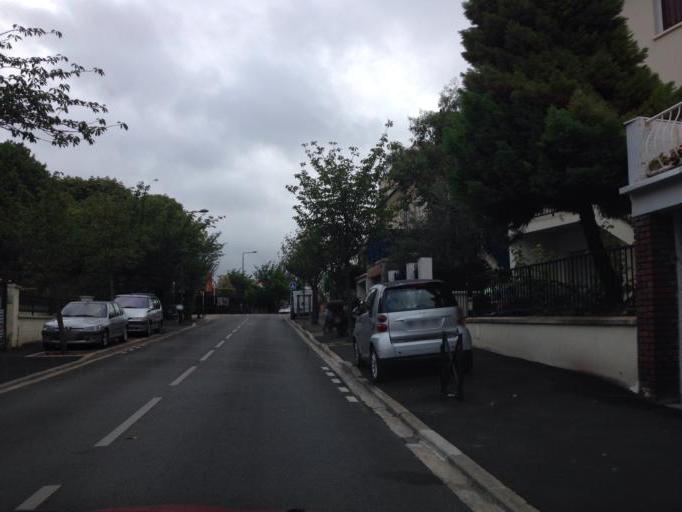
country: FR
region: Ile-de-France
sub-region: Departement des Hauts-de-Seine
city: Meudon
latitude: 48.8134
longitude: 2.2520
